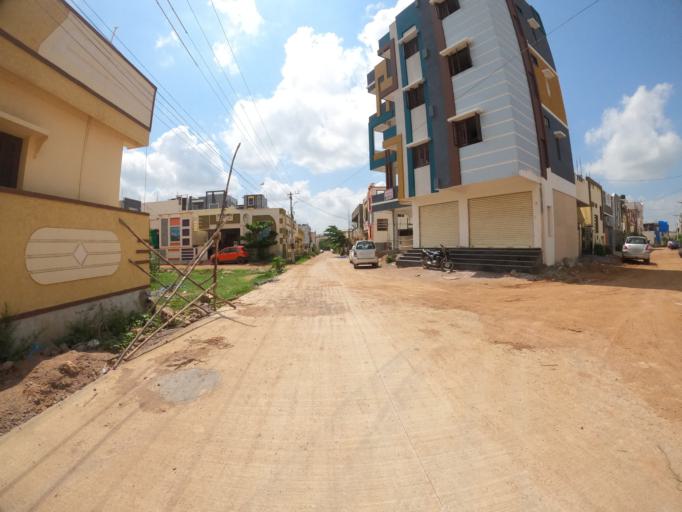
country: IN
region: Telangana
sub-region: Hyderabad
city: Hyderabad
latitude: 17.3629
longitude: 78.3820
